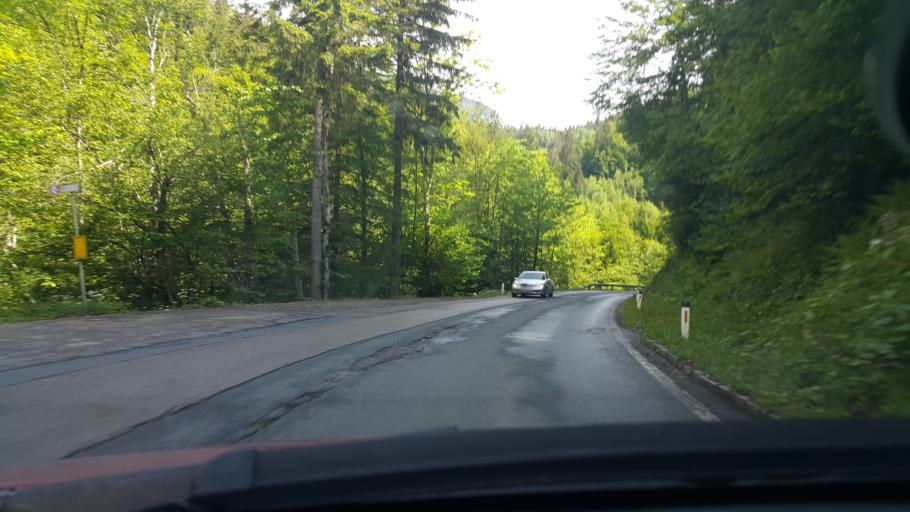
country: AT
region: Carinthia
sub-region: Politischer Bezirk Klagenfurt Land
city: Ferlach
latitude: 46.4705
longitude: 14.2581
